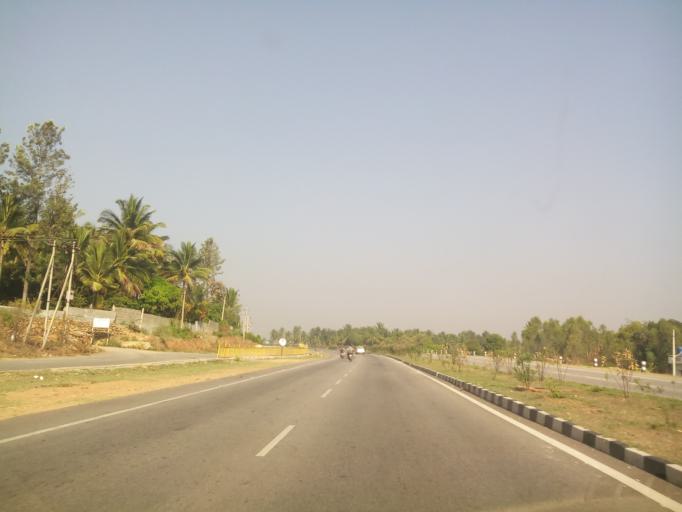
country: IN
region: Karnataka
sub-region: Bangalore Rural
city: Nelamangala
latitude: 13.0652
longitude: 77.3254
